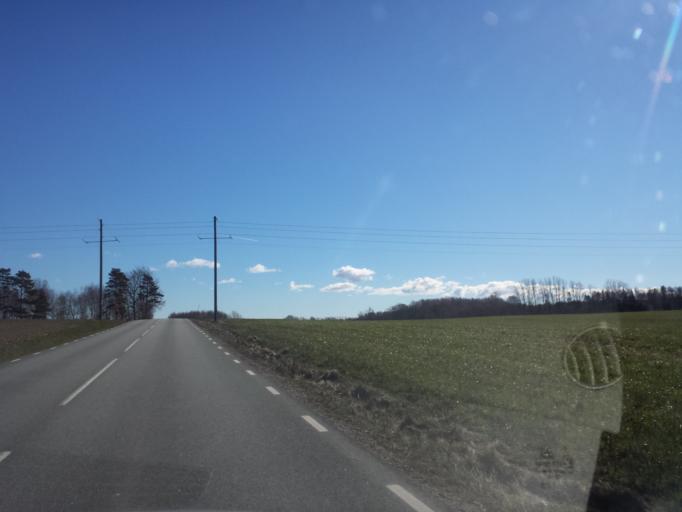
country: SE
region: Skane
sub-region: Sjobo Kommun
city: Sjoebo
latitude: 55.6131
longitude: 13.7816
